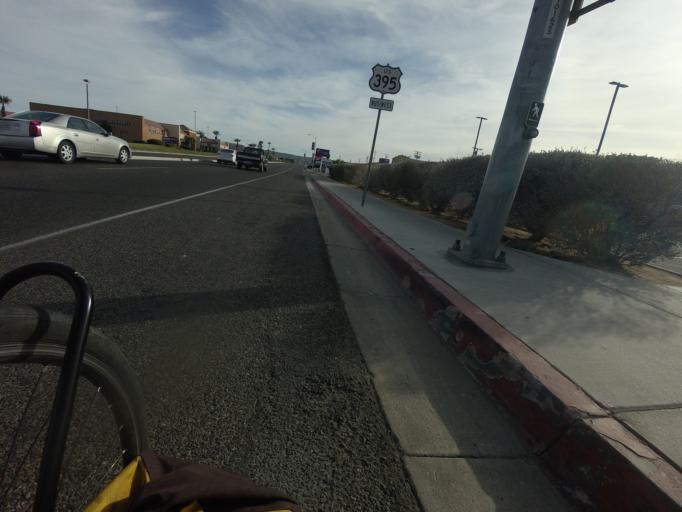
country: US
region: California
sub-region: Kern County
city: Ridgecrest
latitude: 35.6369
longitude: -117.6700
